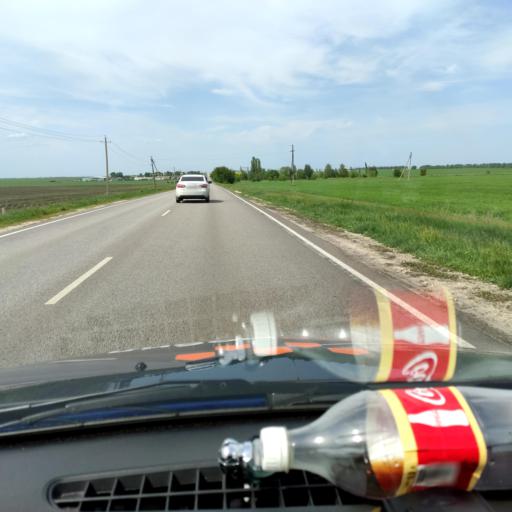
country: RU
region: Voronezj
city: Novaya Usman'
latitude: 51.5676
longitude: 39.3756
